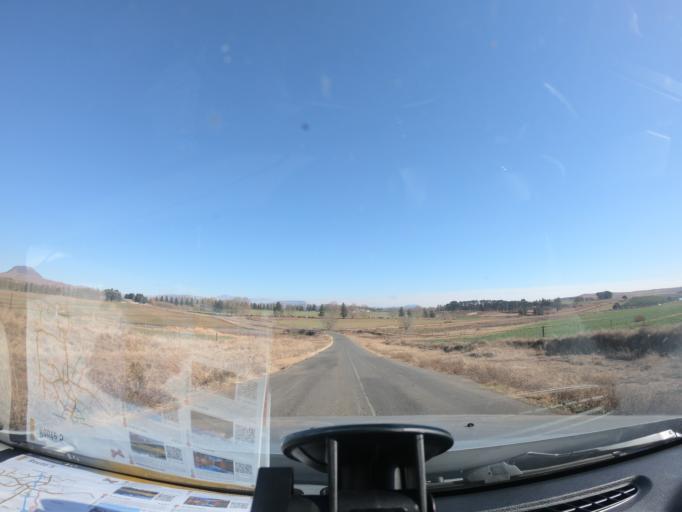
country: ZA
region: KwaZulu-Natal
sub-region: uMgungundlovu District Municipality
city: Mooirivier
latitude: -29.3250
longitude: 29.8350
